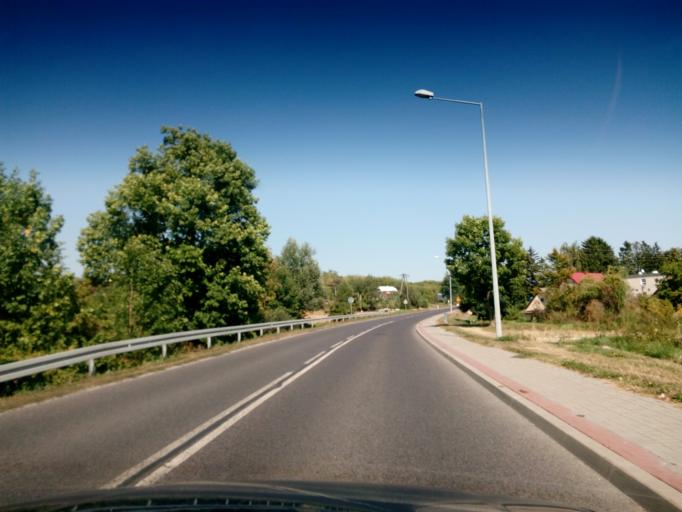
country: PL
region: Lublin Voivodeship
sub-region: Powiat hrubieszowski
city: Horodlo
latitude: 50.8430
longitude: 24.0277
